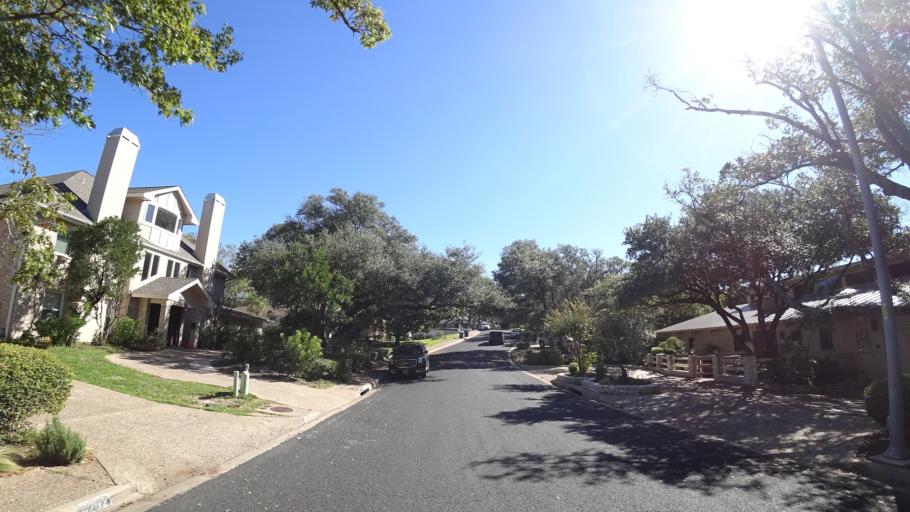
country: US
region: Texas
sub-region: Travis County
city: West Lake Hills
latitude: 30.3512
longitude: -97.7740
